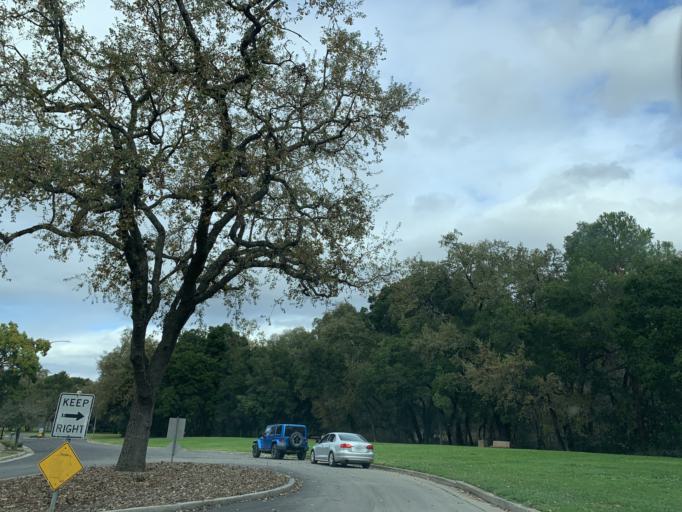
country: US
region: California
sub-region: Santa Clara County
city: Monte Sereno
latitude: 37.2573
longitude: -121.9803
